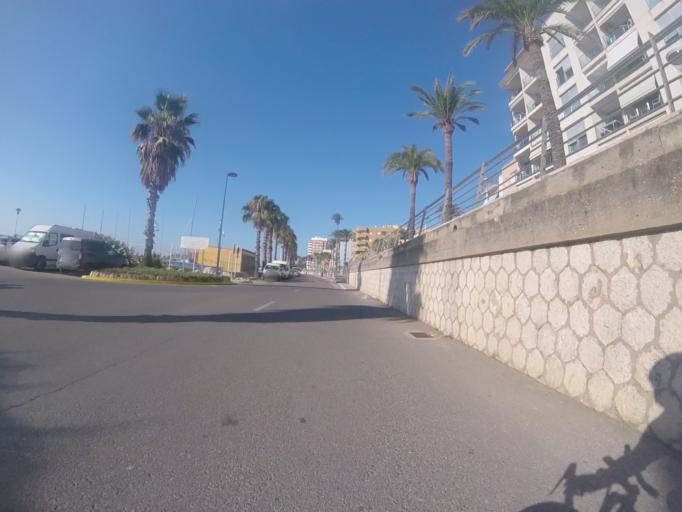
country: ES
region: Valencia
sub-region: Provincia de Castello
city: Benicarlo
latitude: 40.4152
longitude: 0.4323
